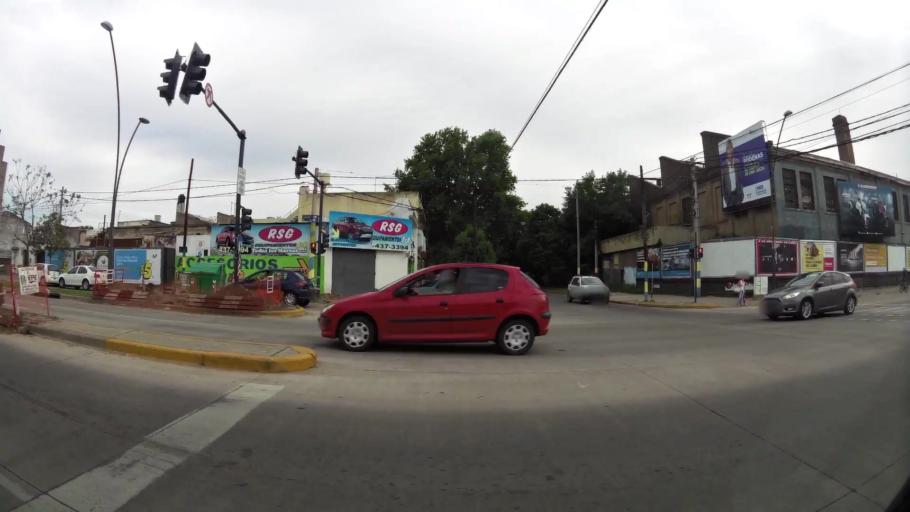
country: AR
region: Santa Fe
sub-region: Departamento de Rosario
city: Rosario
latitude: -32.9219
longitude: -60.6723
